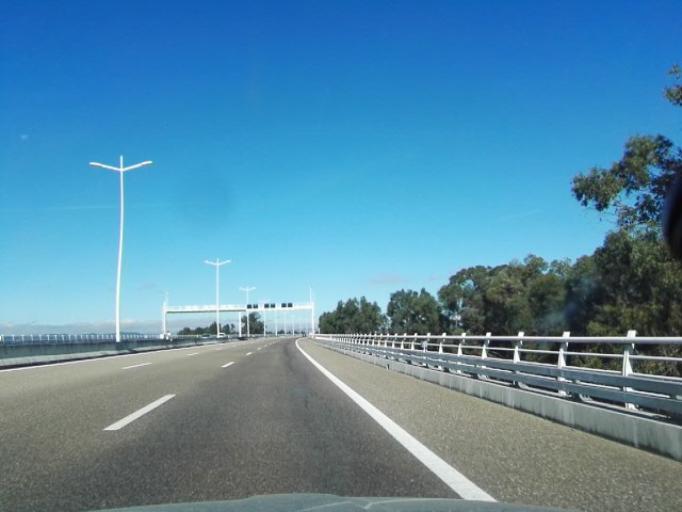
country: PT
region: Santarem
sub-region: Benavente
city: Samora Correia
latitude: 38.9690
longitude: -8.8685
